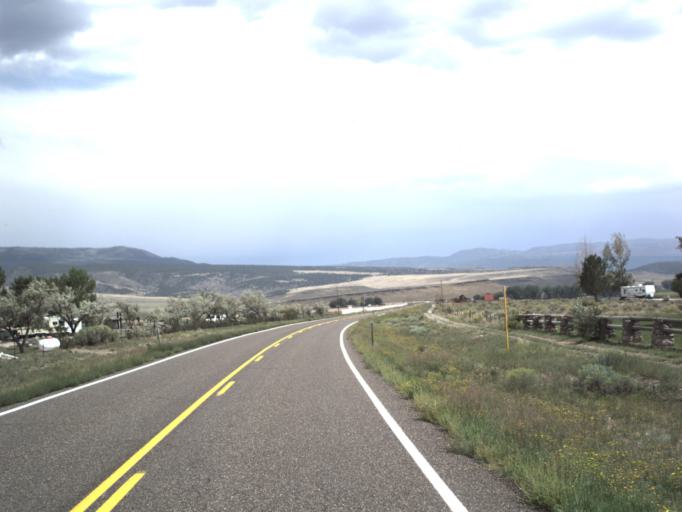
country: US
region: Utah
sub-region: Piute County
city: Junction
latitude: 38.1672
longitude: -112.0204
